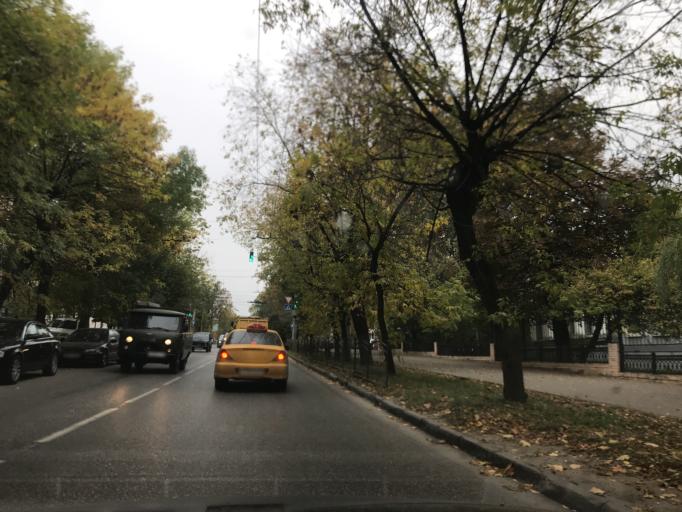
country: RU
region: Kaluga
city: Kaluga
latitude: 54.5198
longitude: 36.2647
